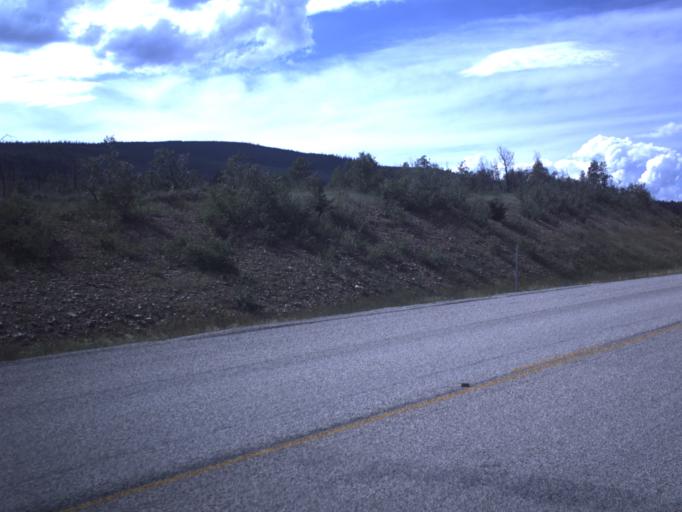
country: US
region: Utah
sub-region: Wasatch County
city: Heber
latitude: 40.2971
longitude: -111.2519
